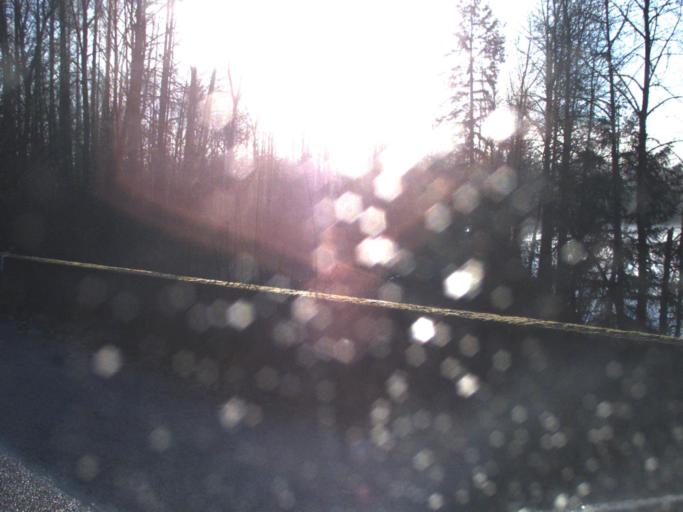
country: US
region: Washington
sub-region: Snohomish County
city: Darrington
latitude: 48.5363
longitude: -121.7405
